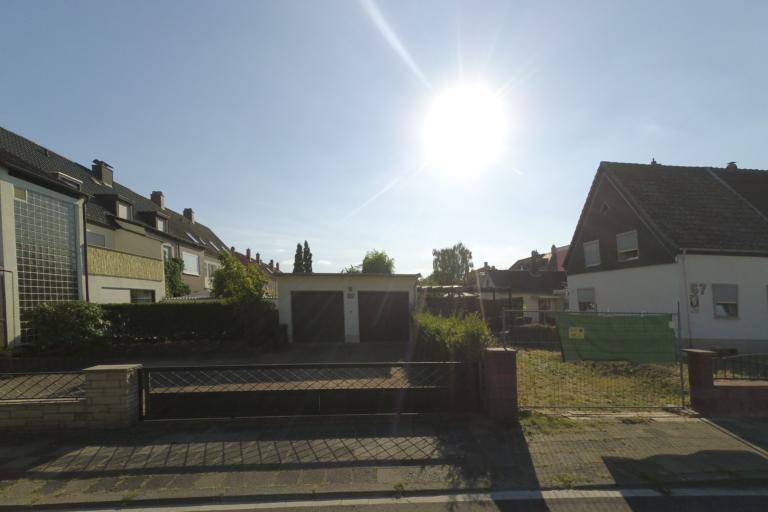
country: DE
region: Rheinland-Pfalz
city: Gartenstadt
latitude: 49.4652
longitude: 8.4038
